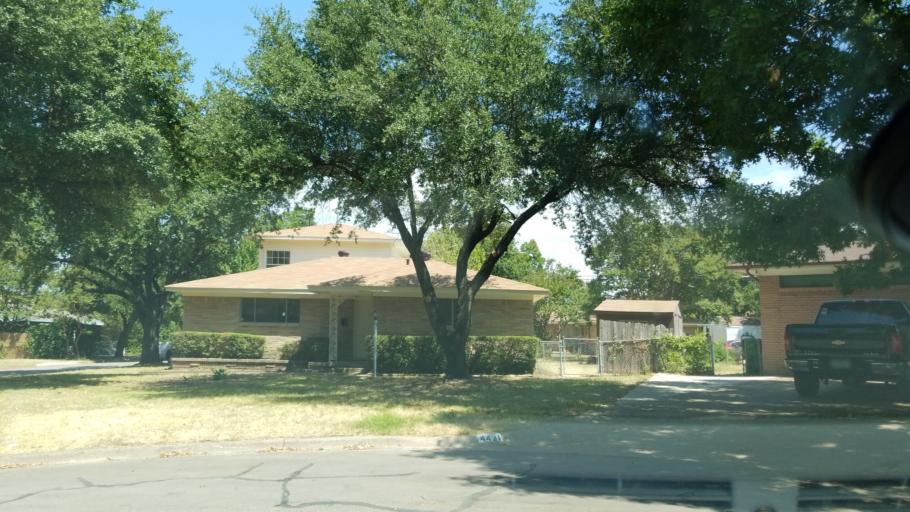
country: US
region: Texas
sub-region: Dallas County
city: Cockrell Hill
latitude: 32.7333
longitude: -96.8927
